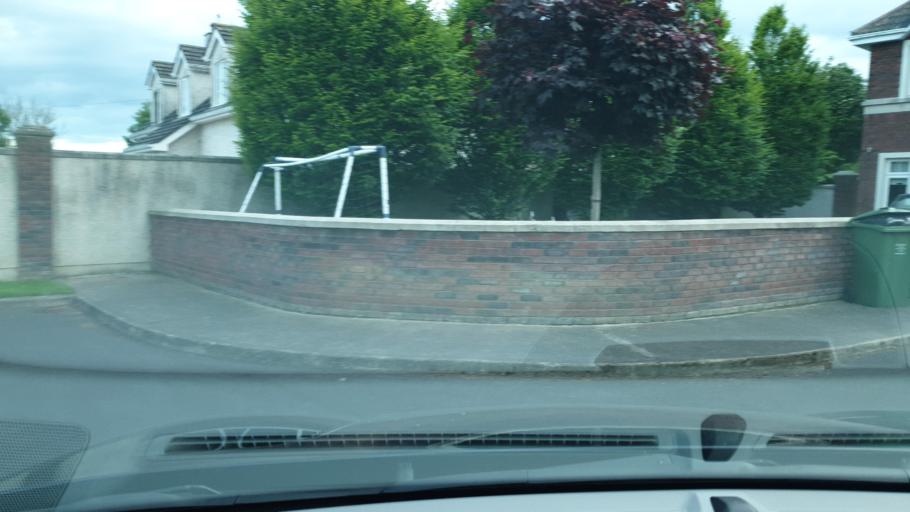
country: IE
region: Leinster
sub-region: An Mhi
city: Ashbourne
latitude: 53.5131
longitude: -6.3848
